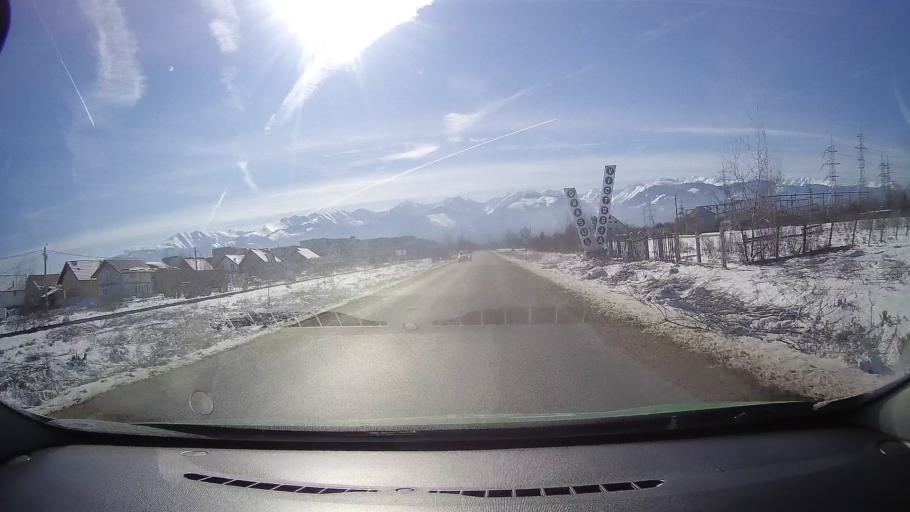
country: RO
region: Brasov
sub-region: Oras Victoria
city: Victoria
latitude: 45.7359
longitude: 24.6950
